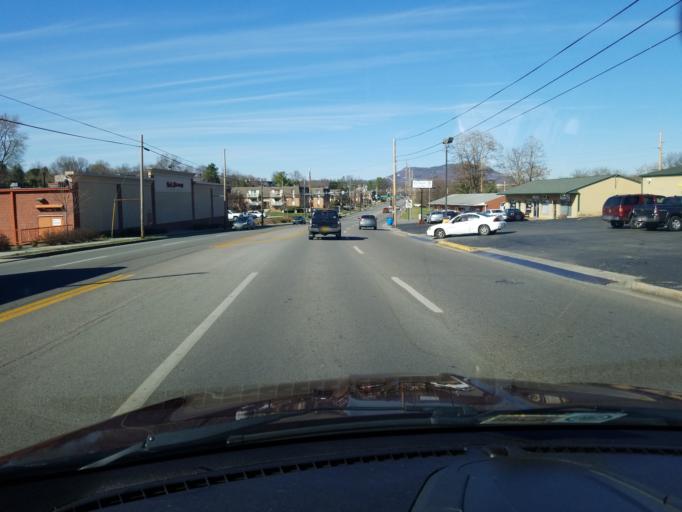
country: US
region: Virginia
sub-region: Roanoke County
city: Hollins
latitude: 37.3128
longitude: -79.9332
